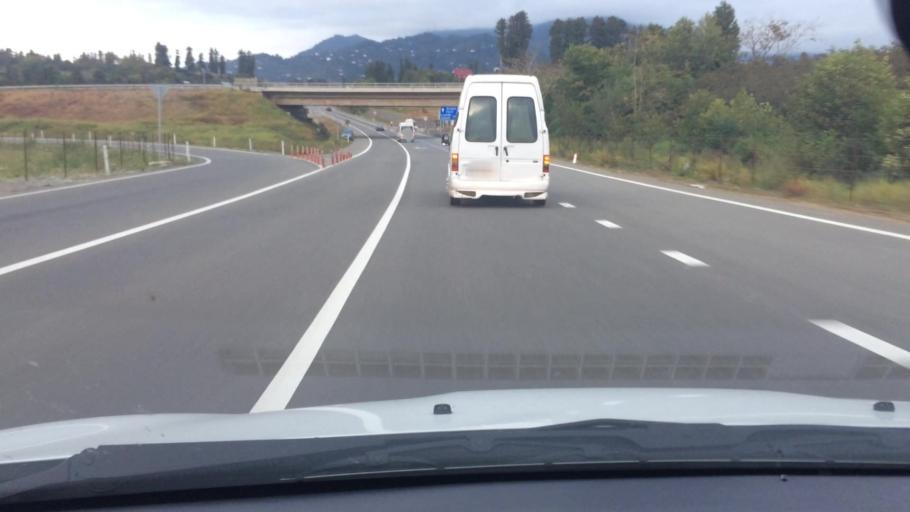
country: GE
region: Ajaria
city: Makhinjauri
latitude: 41.7029
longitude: 41.7362
